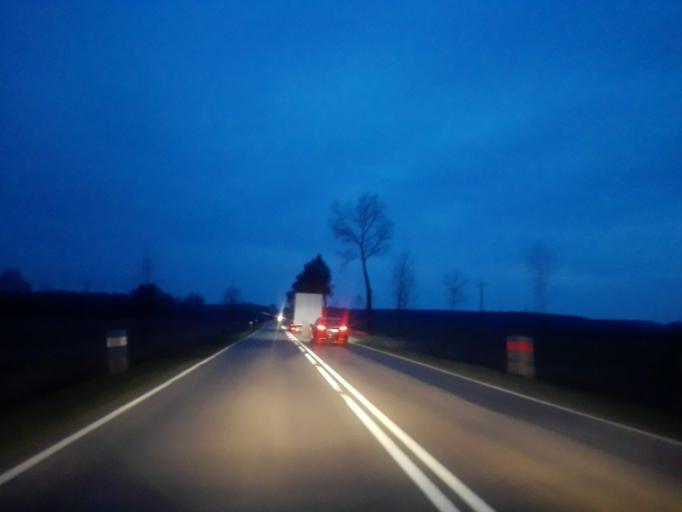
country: PL
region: Podlasie
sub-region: Powiat lomzynski
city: Sniadowo
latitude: 53.0991
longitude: 22.0253
